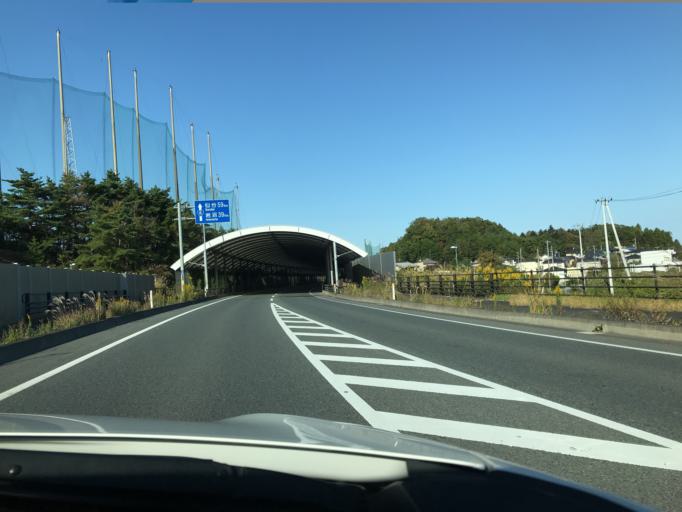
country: JP
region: Miyagi
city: Marumori
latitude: 37.7791
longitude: 140.9397
